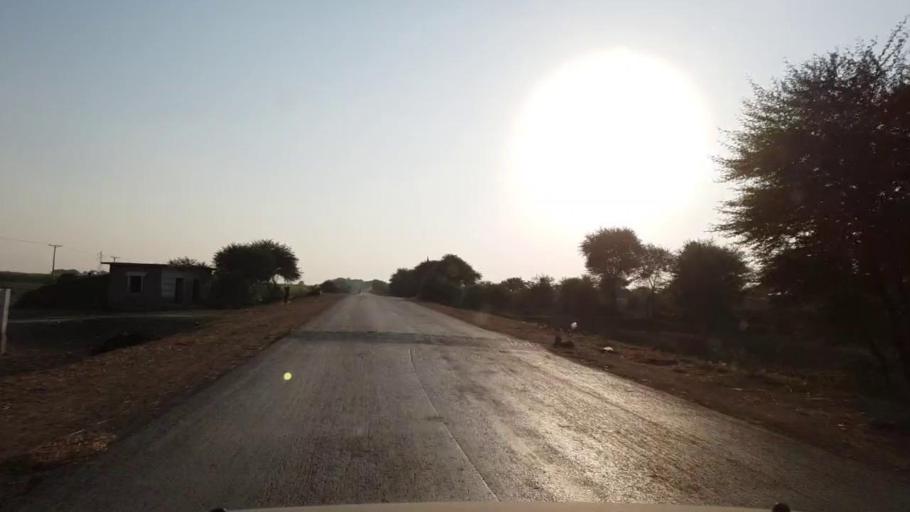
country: PK
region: Sindh
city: Daro Mehar
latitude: 24.6591
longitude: 68.1323
